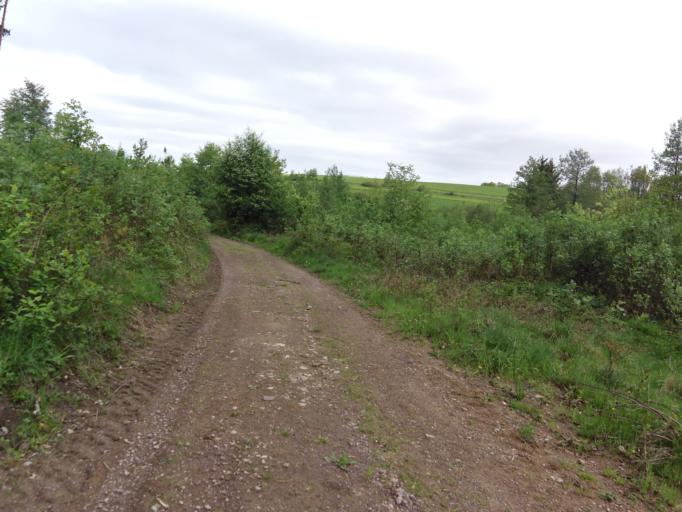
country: DE
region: Thuringia
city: Herrenhof
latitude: 50.8196
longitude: 10.6763
